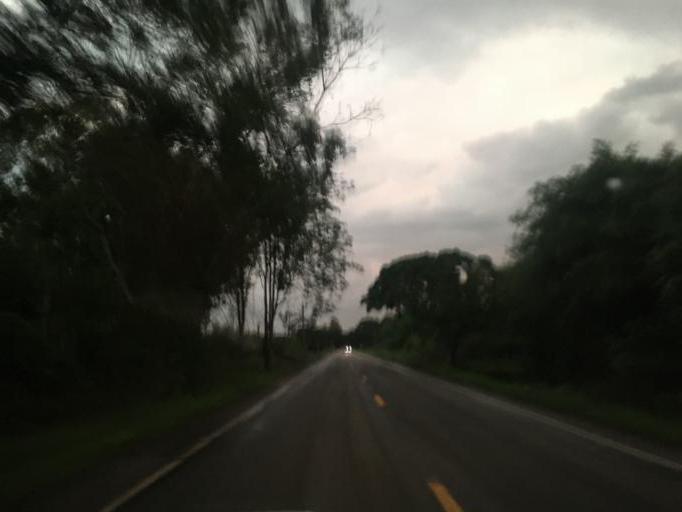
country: TH
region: Changwat Udon Thani
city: Udon Thani
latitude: 17.3463
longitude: 102.7183
